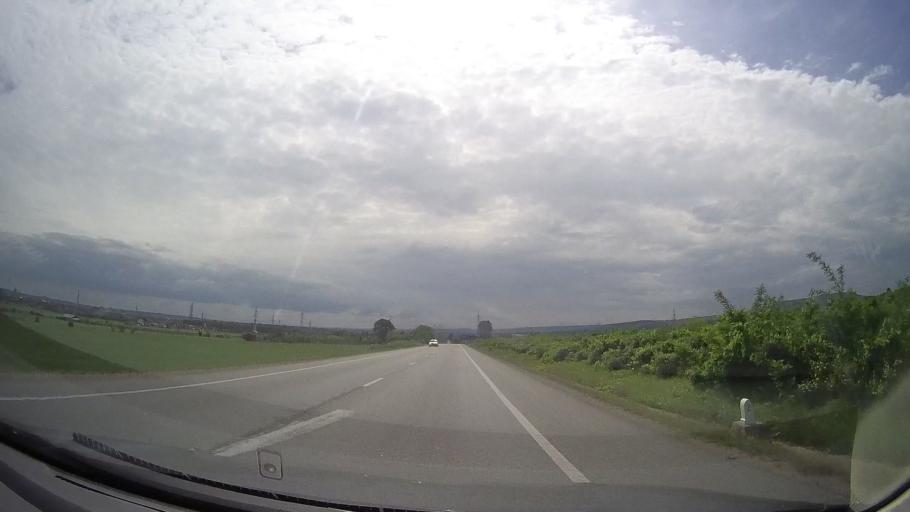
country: RO
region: Mehedinti
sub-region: Municipiul Drobeta-Turnu Severin
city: Drobeta-Turnu Severin
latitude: 44.6572
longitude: 22.6581
